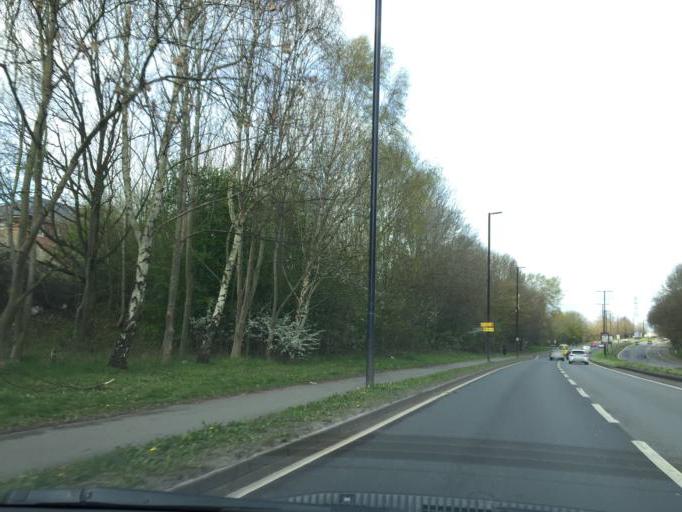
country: GB
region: England
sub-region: Coventry
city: Coventry
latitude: 52.3939
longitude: -1.5531
